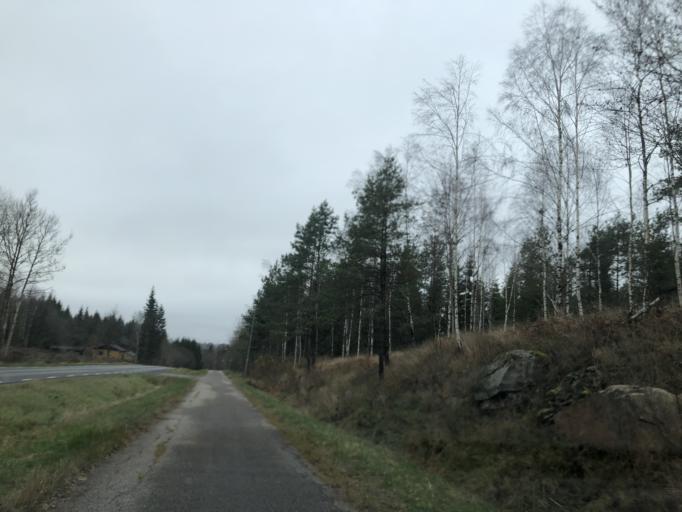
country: SE
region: Vaestra Goetaland
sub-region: Ulricehamns Kommun
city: Ulricehamn
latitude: 57.6723
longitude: 13.4474
